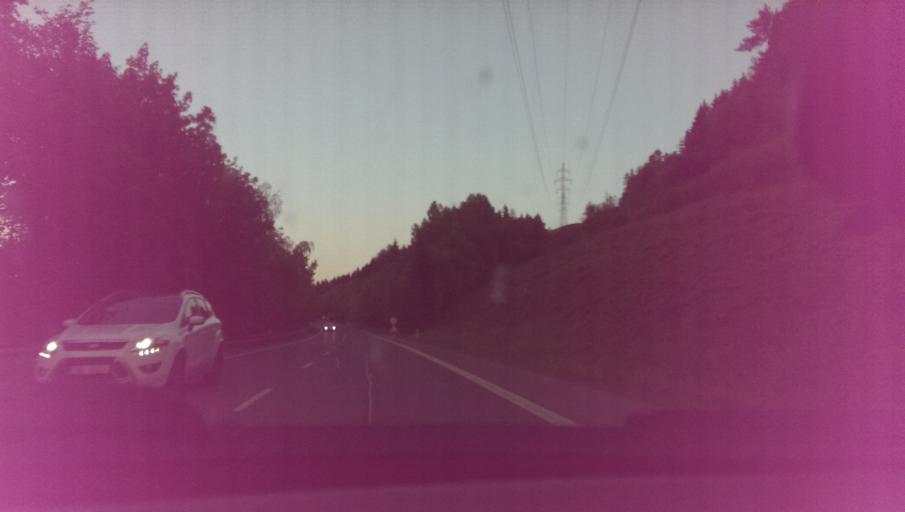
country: CZ
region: Zlin
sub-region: Okres Vsetin
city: Vsetin
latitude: 49.3384
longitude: 17.9776
